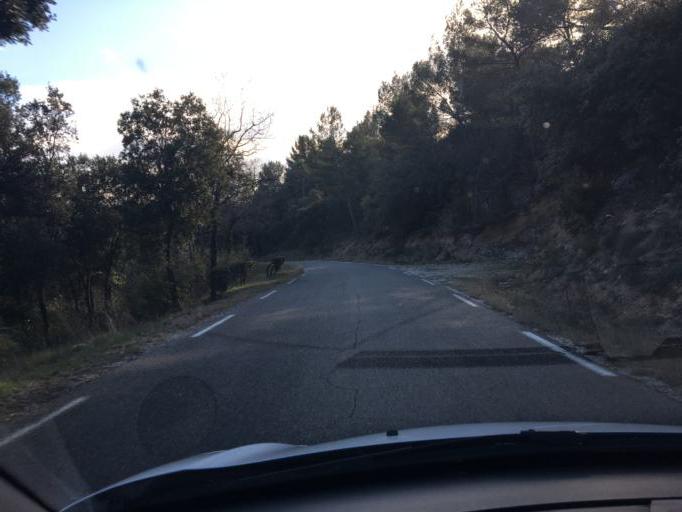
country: FR
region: Provence-Alpes-Cote d'Azur
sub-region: Departement du Vaucluse
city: Villes-sur-Auzon
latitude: 44.0558
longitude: 5.2449
